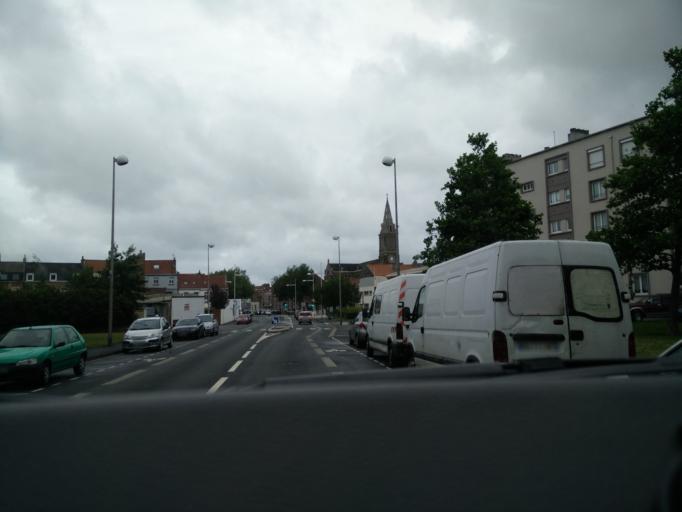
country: FR
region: Nord-Pas-de-Calais
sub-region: Departement du Nord
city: Coudekerque-Branche
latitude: 51.0398
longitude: 2.4056
